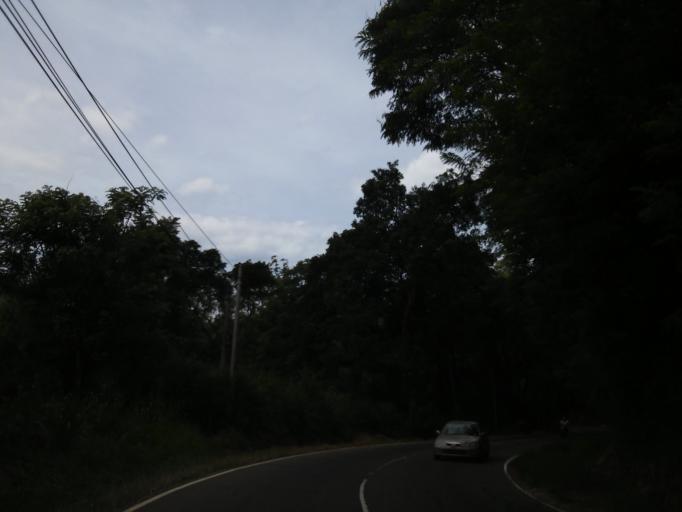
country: LK
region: Uva
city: Haputale
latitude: 6.8708
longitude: 80.9519
